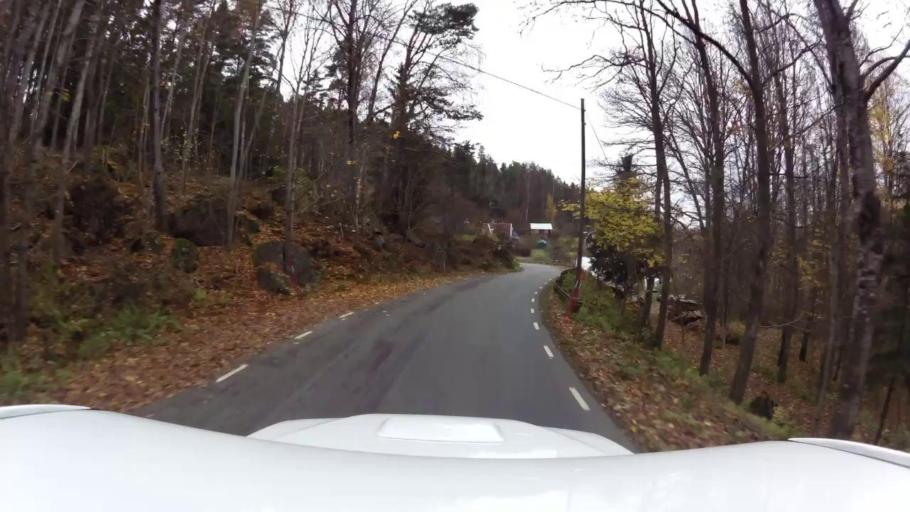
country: SE
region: OEstergoetland
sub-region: Kinda Kommun
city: Rimforsa
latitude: 58.1411
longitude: 15.6332
